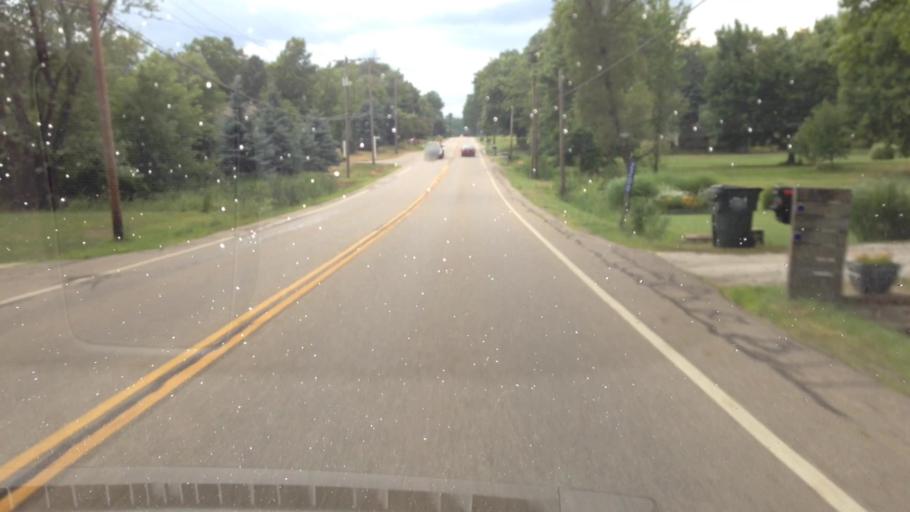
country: US
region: Ohio
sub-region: Stark County
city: Uniontown
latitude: 40.9752
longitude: -81.4442
